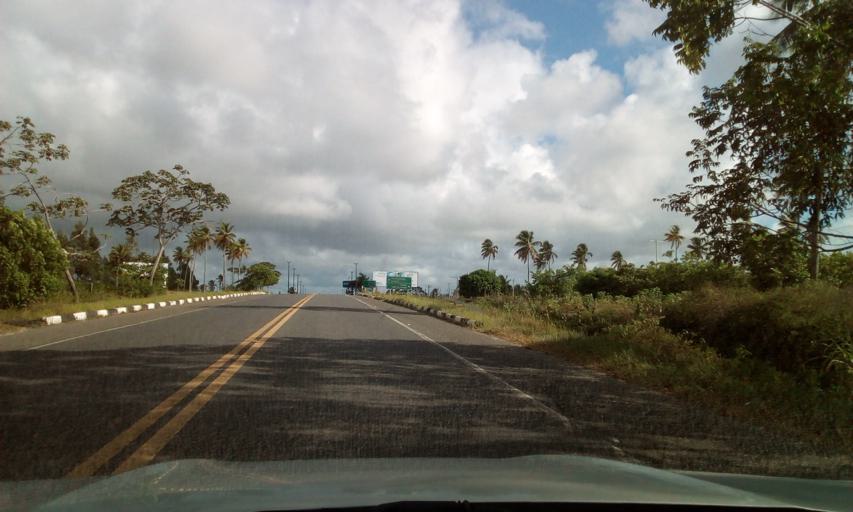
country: BR
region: Bahia
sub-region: Conde
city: Conde
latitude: -11.8285
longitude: -37.6354
